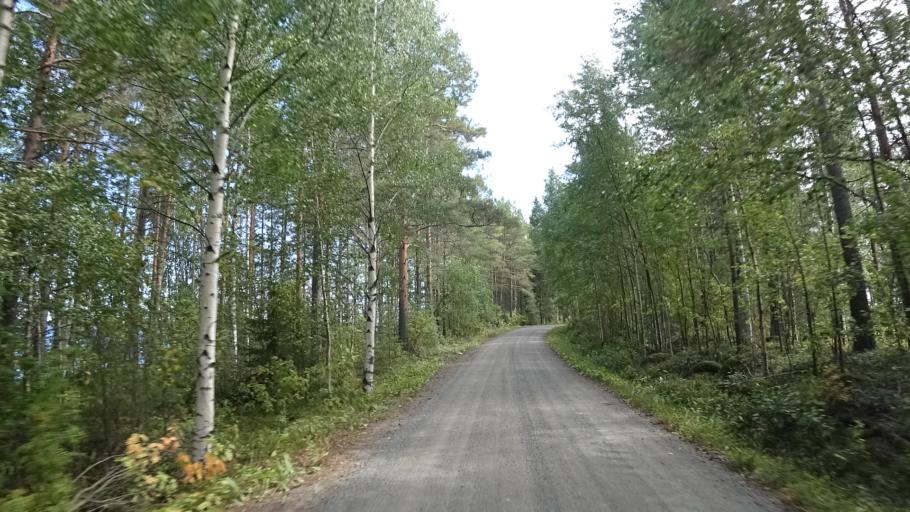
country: FI
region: North Karelia
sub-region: Keski-Karjala
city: Raeaekkylae
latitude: 62.3949
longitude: 29.7674
